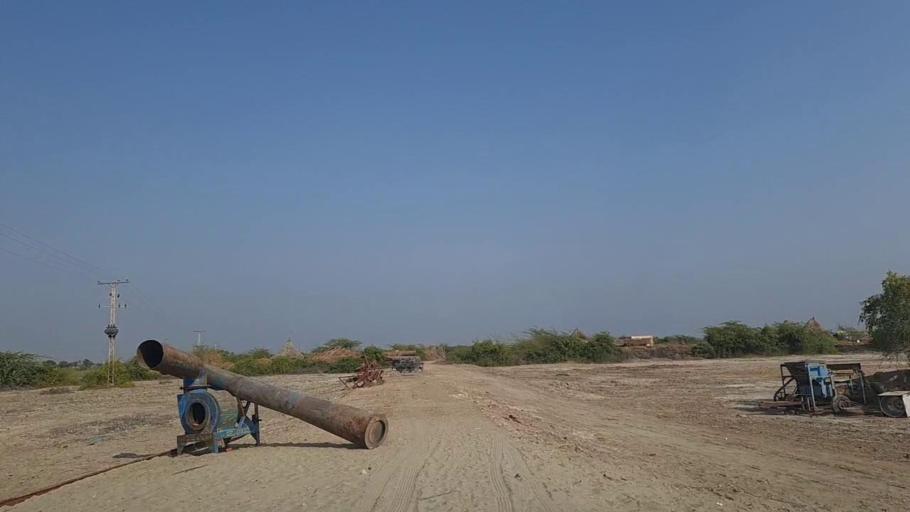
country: PK
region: Sindh
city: Dhoro Naro
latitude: 25.4846
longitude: 69.5276
